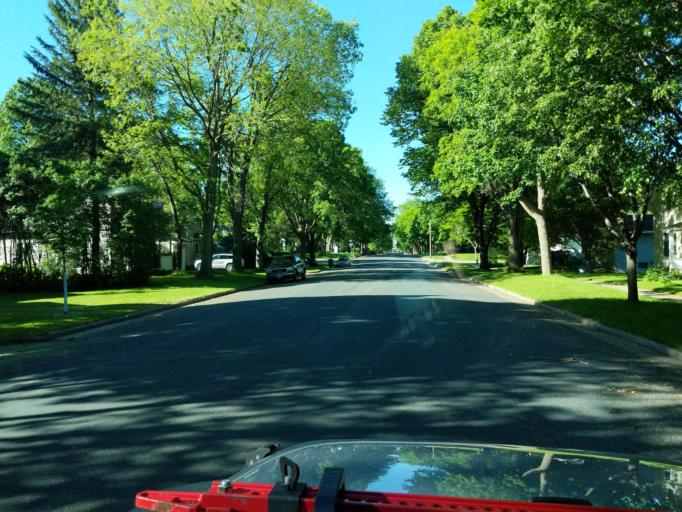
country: US
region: Wisconsin
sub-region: Pierce County
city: River Falls
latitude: 44.8618
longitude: -92.6211
